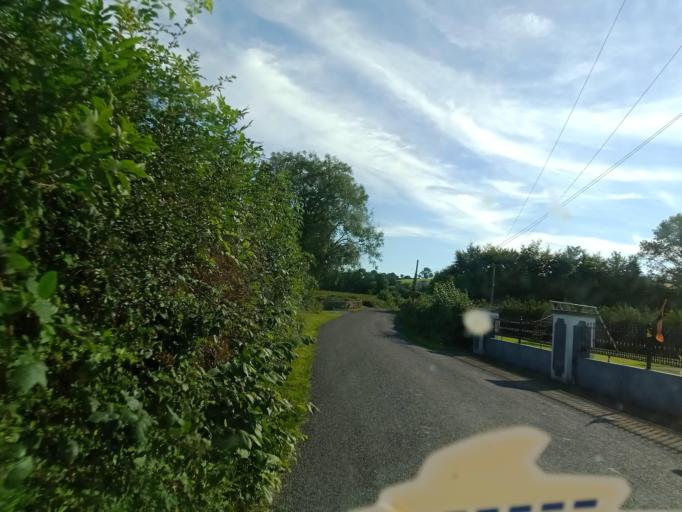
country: IE
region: Leinster
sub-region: Kilkenny
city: Ballyragget
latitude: 52.7714
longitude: -7.3900
